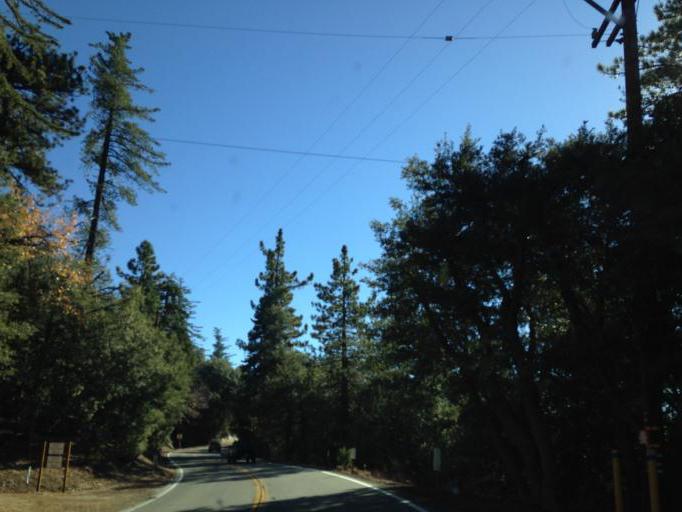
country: US
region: California
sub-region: Riverside County
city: Idyllwild-Pine Cove
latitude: 33.7706
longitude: -116.7409
